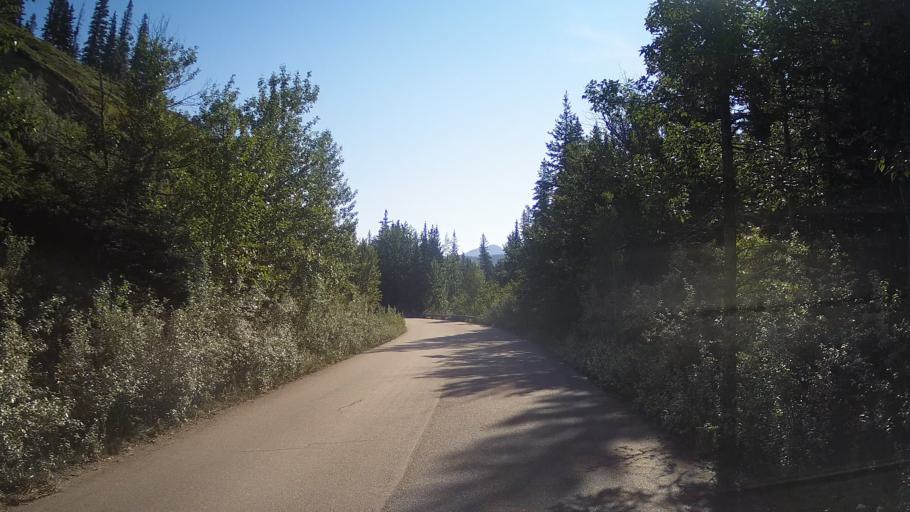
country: CA
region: Alberta
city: Jasper Park Lodge
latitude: 53.1991
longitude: -117.9210
